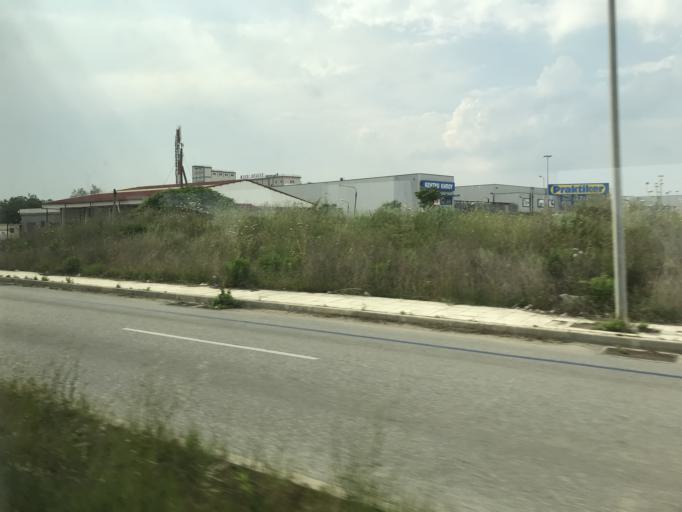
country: GR
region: East Macedonia and Thrace
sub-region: Nomos Evrou
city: Alexandroupoli
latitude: 40.8550
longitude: 25.9245
